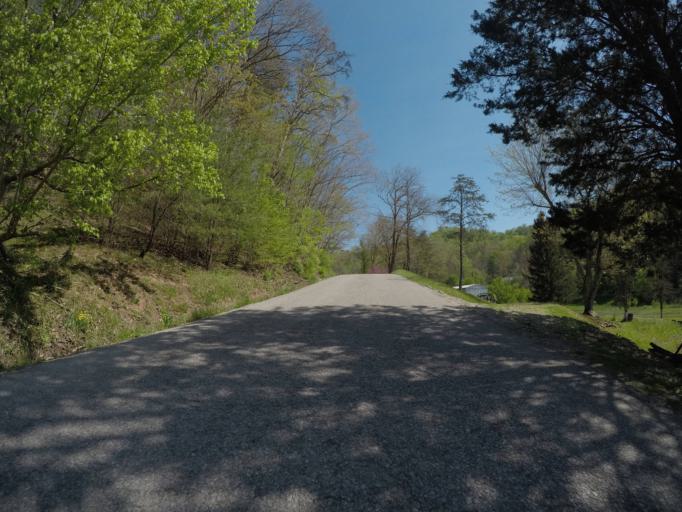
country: US
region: West Virginia
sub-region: Kanawha County
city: Charleston
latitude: 38.4147
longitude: -81.6125
